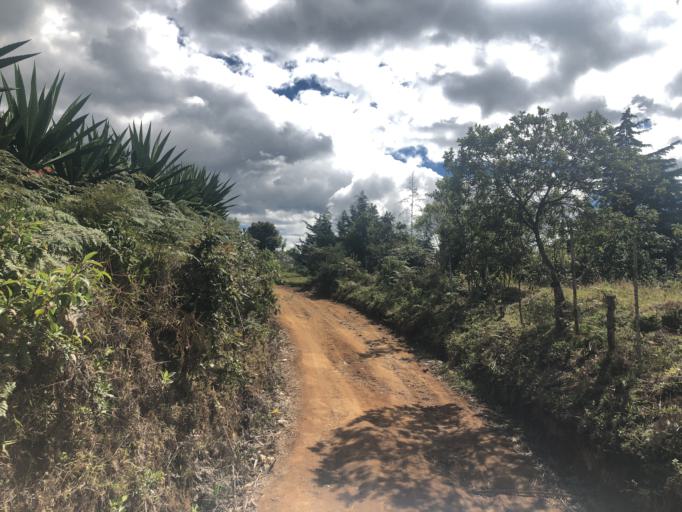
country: CO
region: Cauca
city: Silvia
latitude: 2.6793
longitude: -76.4423
